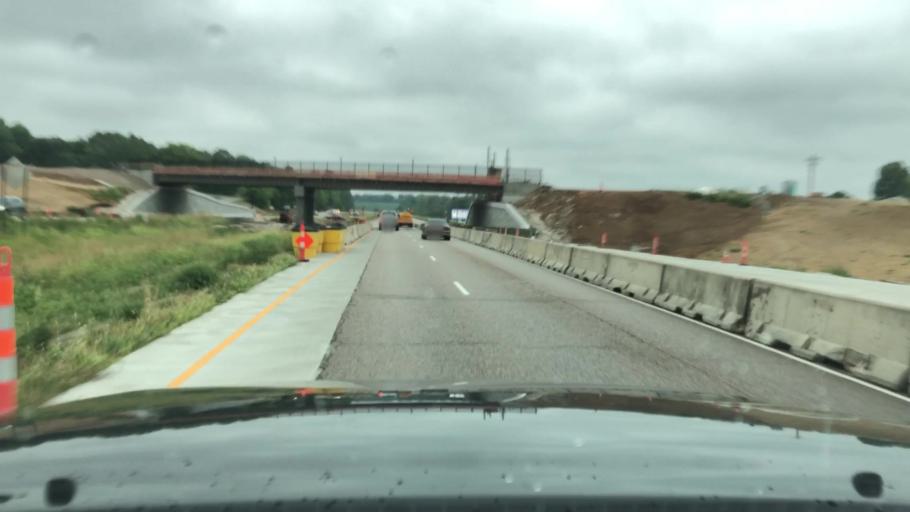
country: US
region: Missouri
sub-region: Saint Charles County
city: Wentzville
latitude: 38.8531
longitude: -90.8696
